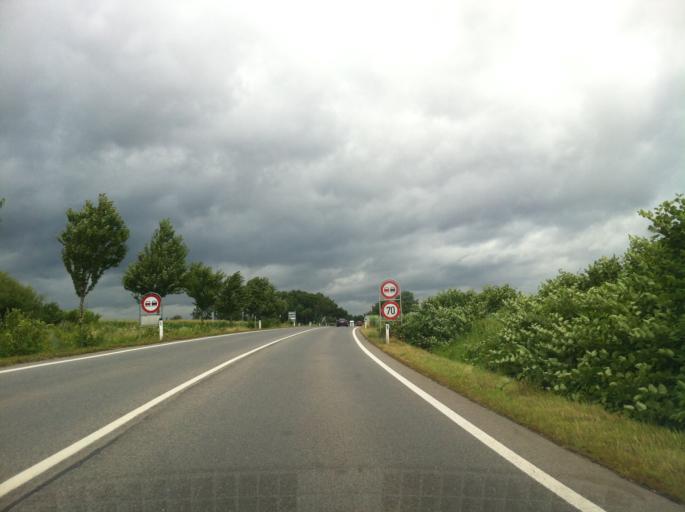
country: AT
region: Lower Austria
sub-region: Politischer Bezirk Tulln
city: Langenrohr
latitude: 48.2962
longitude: 16.0078
